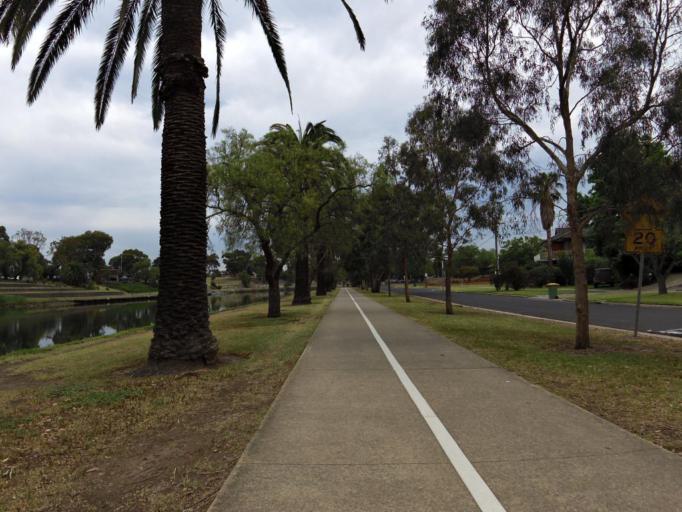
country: AU
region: Victoria
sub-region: Moonee Valley
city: Moonee Ponds
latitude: -37.7666
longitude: 144.9015
